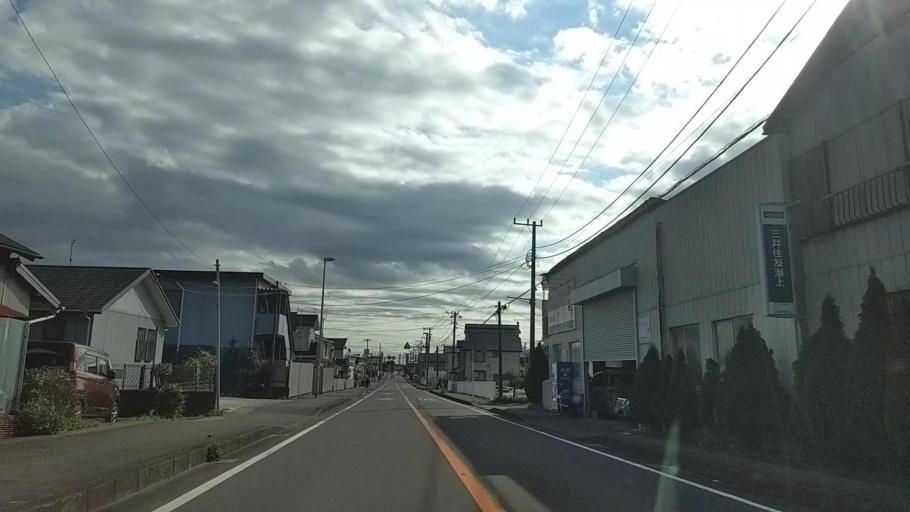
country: JP
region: Kanagawa
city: Ninomiya
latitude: 35.2883
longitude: 139.2043
